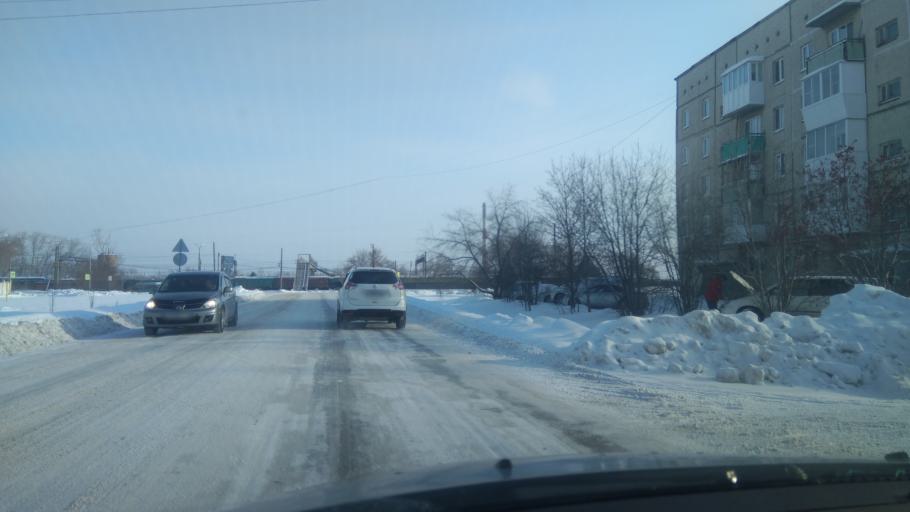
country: RU
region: Sverdlovsk
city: Sukhoy Log
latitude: 56.8910
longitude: 62.0403
